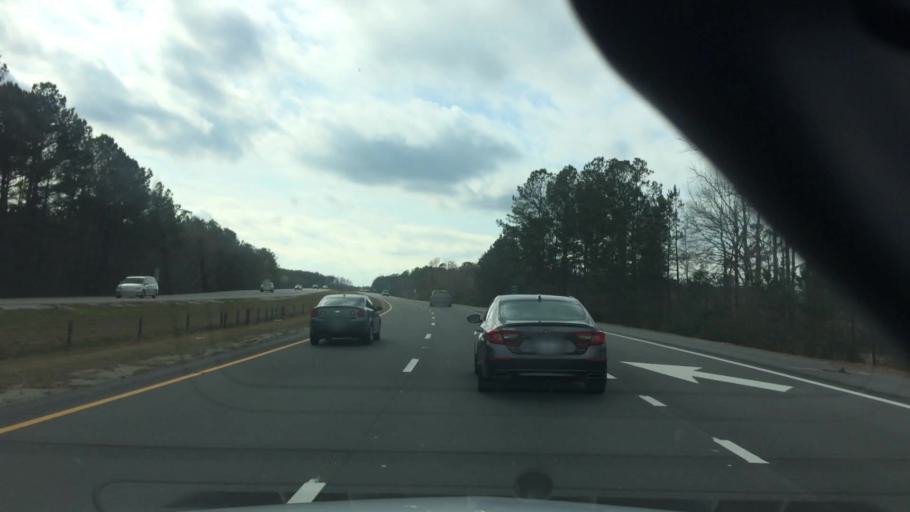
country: US
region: North Carolina
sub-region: New Hanover County
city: Skippers Corner
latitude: 34.3172
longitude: -77.8851
